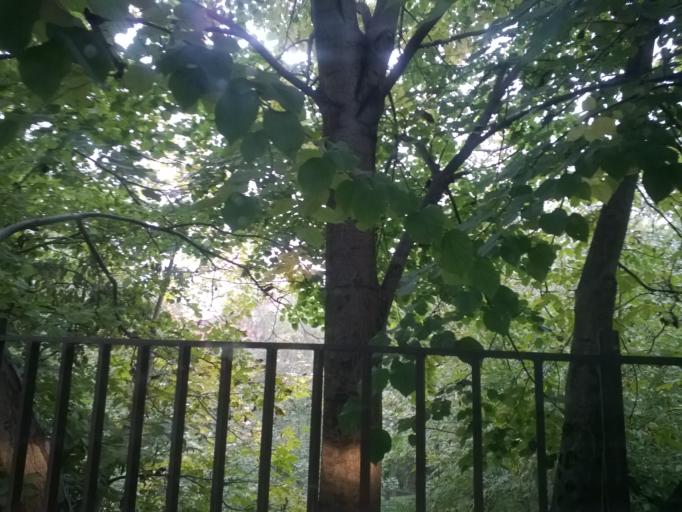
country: RS
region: Central Serbia
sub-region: Belgrade
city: Zvezdara
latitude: 44.7927
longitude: 20.5274
